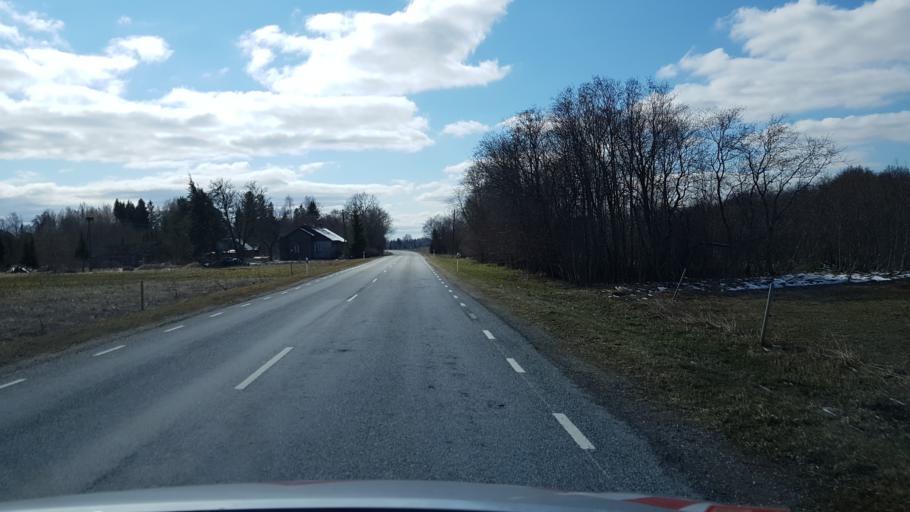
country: EE
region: Laeaene-Virumaa
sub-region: Tapa vald
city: Tapa
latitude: 59.3433
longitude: 26.0033
